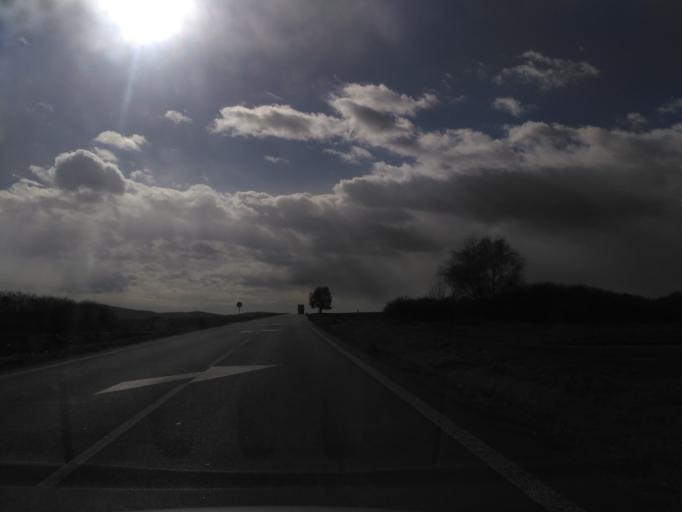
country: SK
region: Kosicky
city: Trebisov
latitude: 48.5795
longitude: 21.7060
